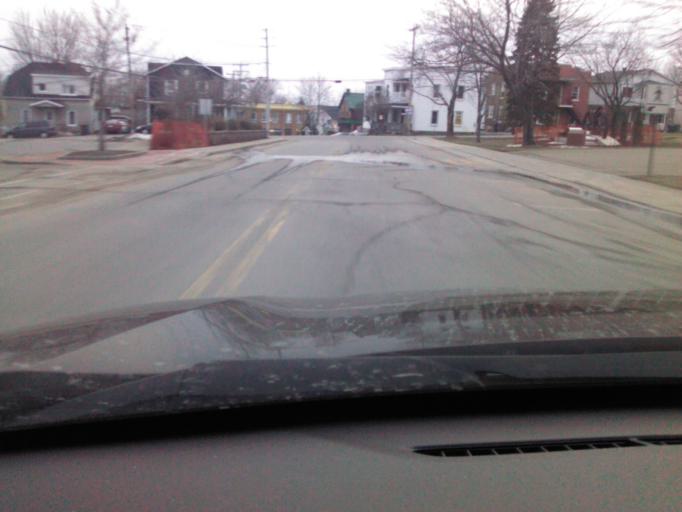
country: CA
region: Quebec
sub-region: Capitale-Nationale
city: Donnacona
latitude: 46.6743
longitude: -71.7392
